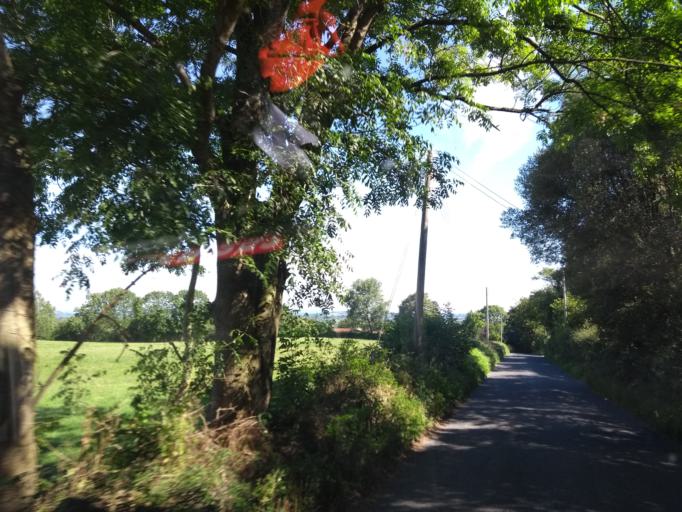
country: GB
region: England
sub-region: Somerset
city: Ilchester
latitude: 51.0798
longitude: -2.6442
